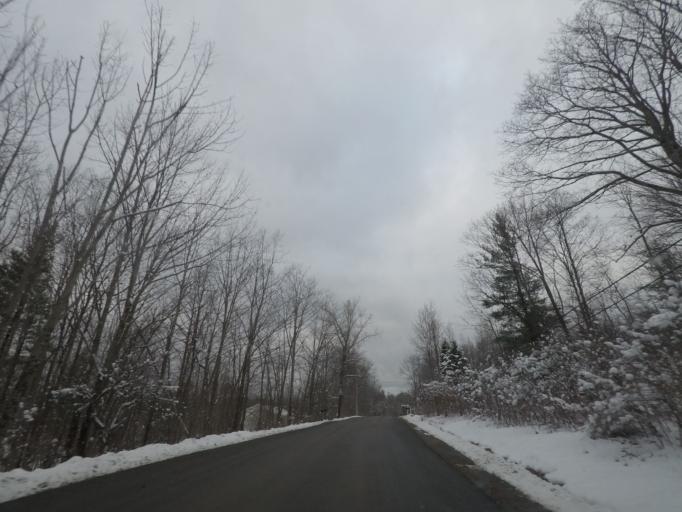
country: US
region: New York
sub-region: Rensselaer County
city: Averill Park
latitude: 42.6622
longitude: -73.5330
